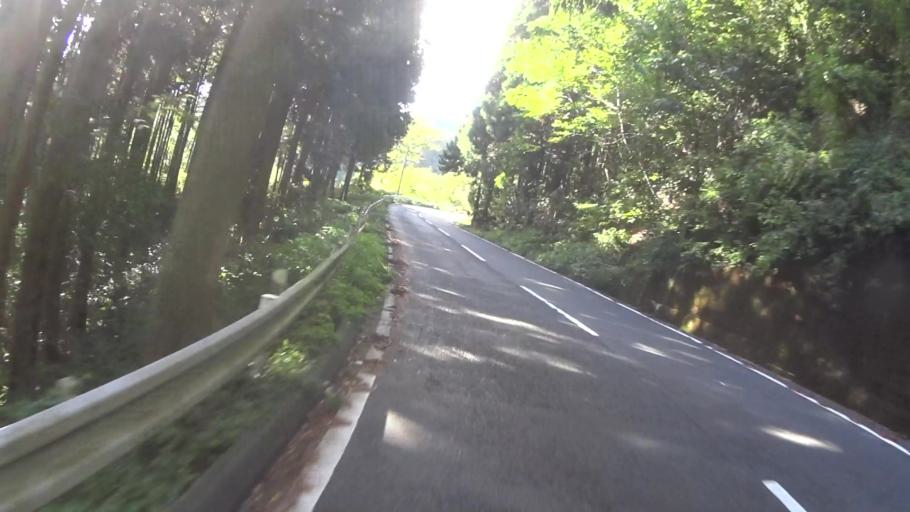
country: JP
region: Kyoto
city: Maizuru
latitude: 35.5401
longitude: 135.4511
